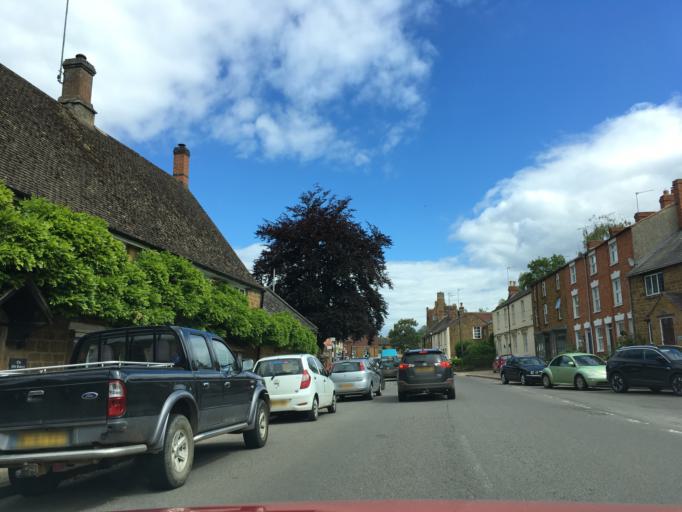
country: GB
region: England
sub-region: Oxfordshire
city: Bloxham
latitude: 52.0208
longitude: -1.3742
